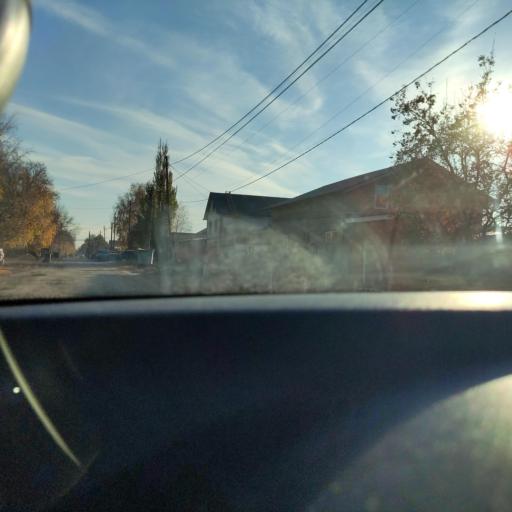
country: RU
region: Samara
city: Petra-Dubrava
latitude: 53.2573
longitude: 50.3245
